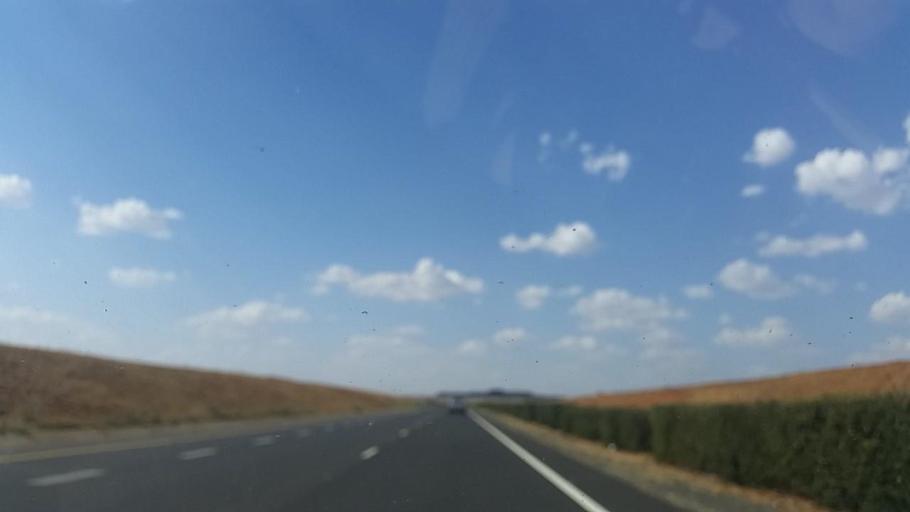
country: ZA
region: Orange Free State
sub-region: Mangaung Metropolitan Municipality
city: Bloemfontein
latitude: -29.1972
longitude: 26.1920
